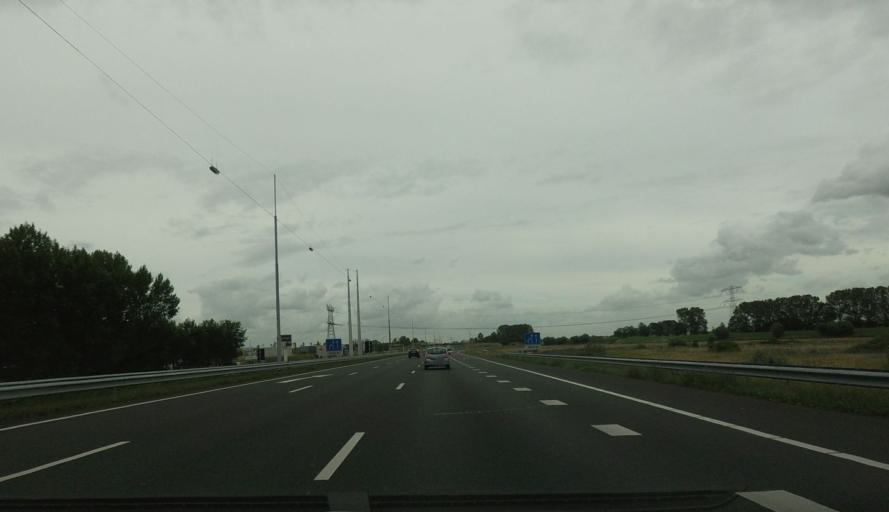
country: NL
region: North Holland
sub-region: Gemeente Beverwijk
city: Beverwijk
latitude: 52.4696
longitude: 4.6784
